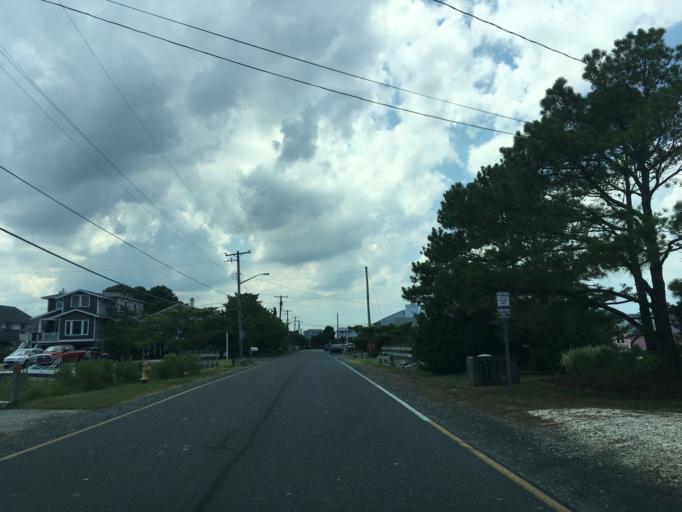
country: US
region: Delaware
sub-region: Sussex County
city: Bethany Beach
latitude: 38.4596
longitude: -75.0539
